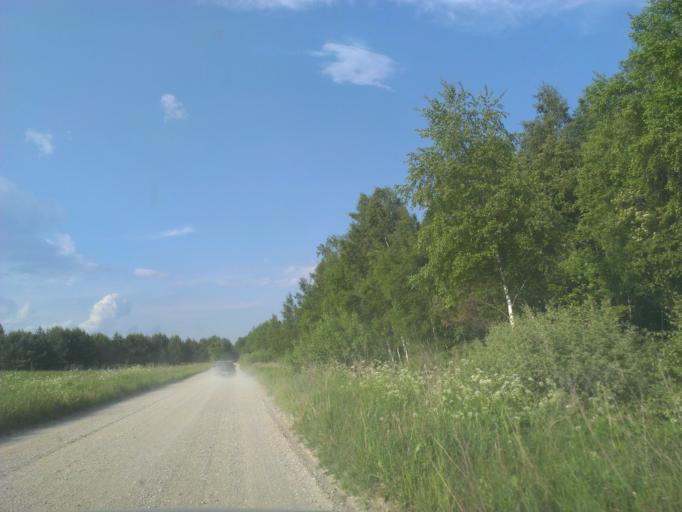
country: LT
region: Klaipedos apskritis
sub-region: Palanga
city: Sventoji
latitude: 56.0257
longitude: 21.2190
